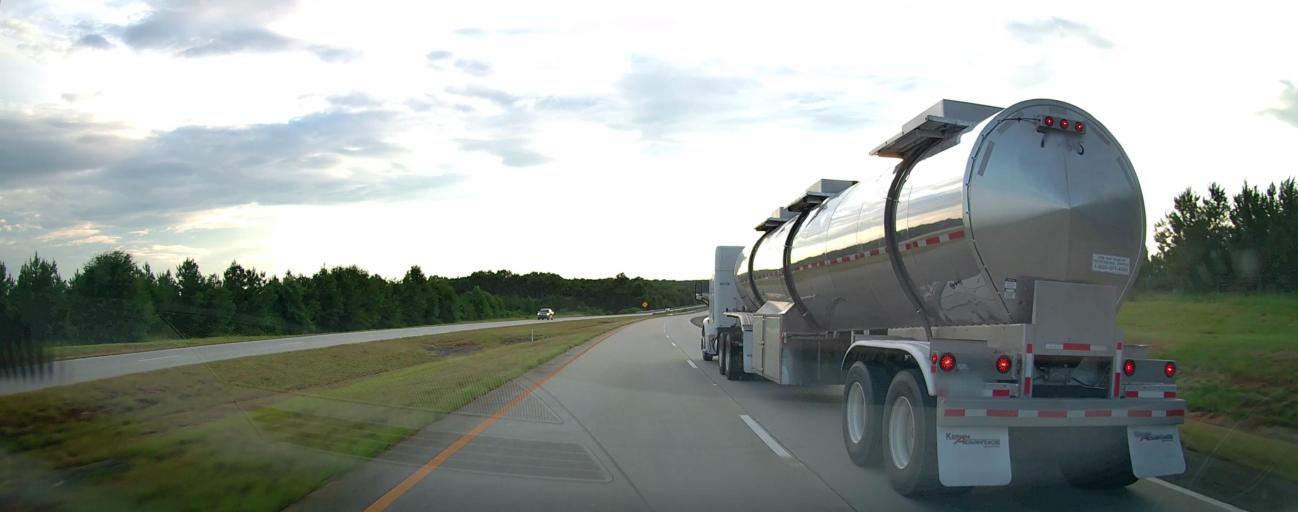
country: US
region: Georgia
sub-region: Taylor County
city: Reynolds
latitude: 32.5458
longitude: -83.9938
